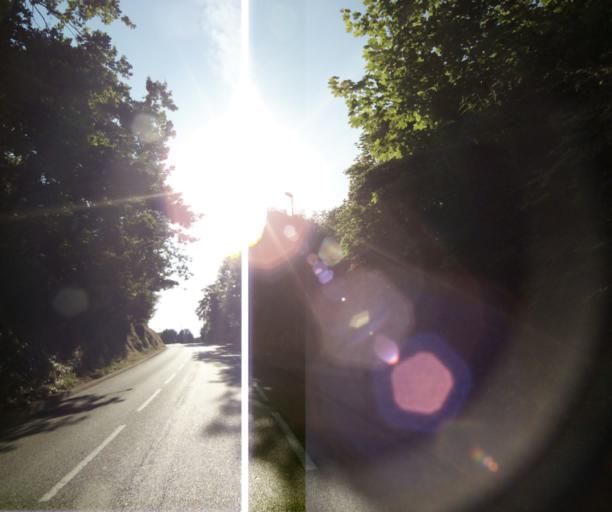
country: FR
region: Pays de la Loire
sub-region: Departement de la Mayenne
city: Laval
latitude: 48.0648
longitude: -0.7855
